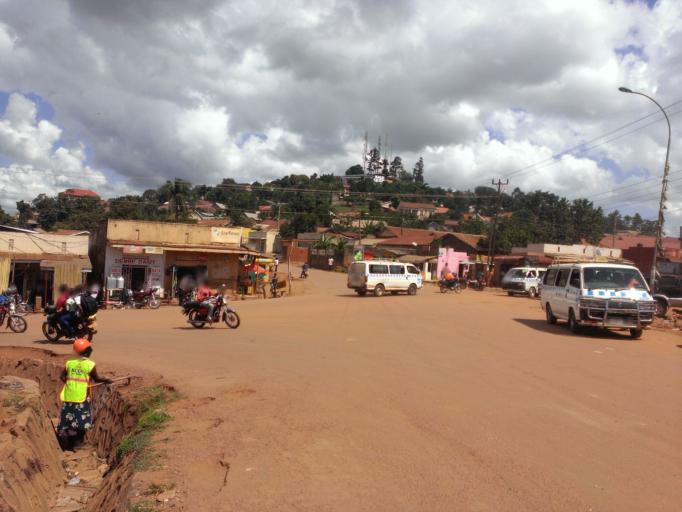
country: UG
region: Central Region
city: Kampala Central Division
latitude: 0.3294
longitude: 32.5499
